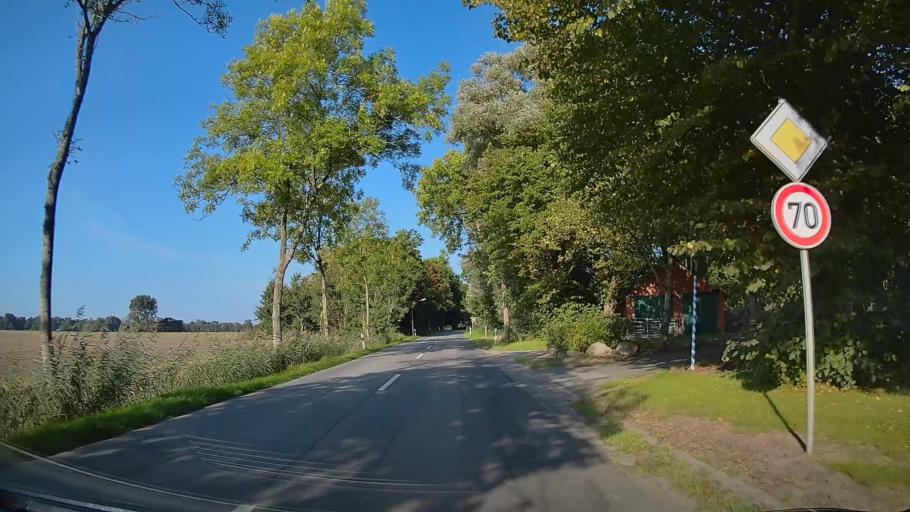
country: DE
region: Lower Saxony
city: Cappel
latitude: 53.7458
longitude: 8.5567
